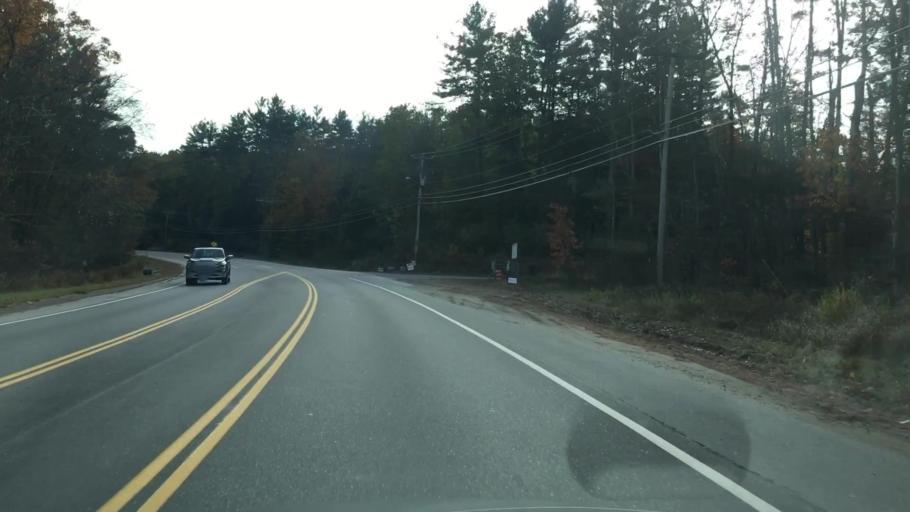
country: US
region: New Hampshire
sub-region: Hillsborough County
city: Mont Vernon
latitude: 42.8913
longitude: -71.6093
